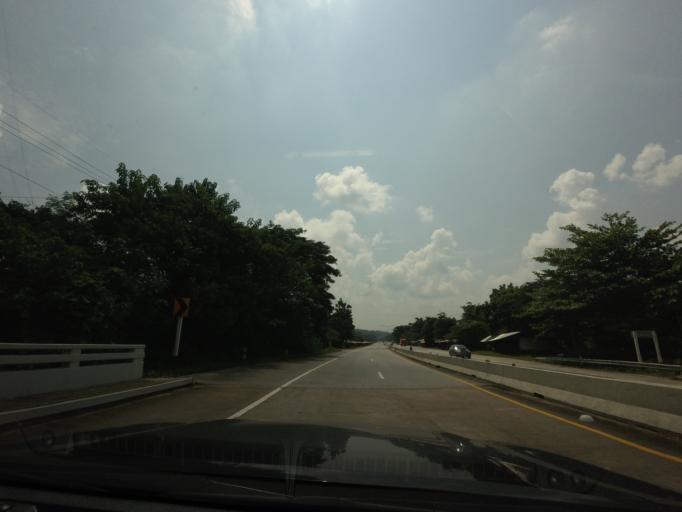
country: TH
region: Uttaradit
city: Lap Lae
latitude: 17.7996
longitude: 100.1155
